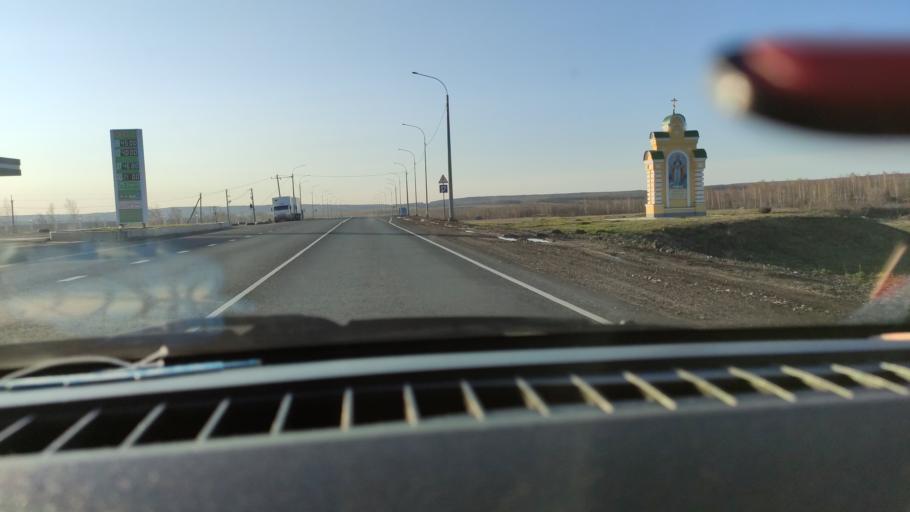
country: RU
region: Saratov
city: Shikhany
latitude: 52.1314
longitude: 47.2284
